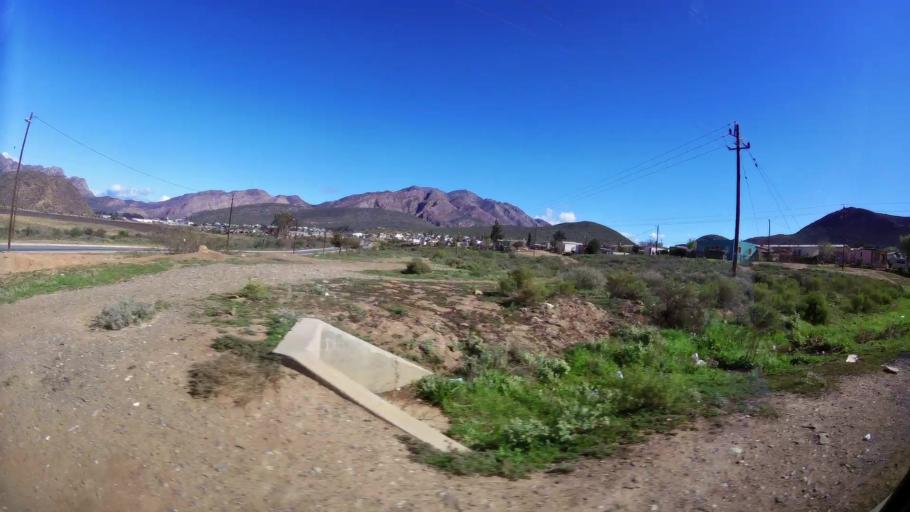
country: ZA
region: Western Cape
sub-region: Cape Winelands District Municipality
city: Ashton
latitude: -33.7687
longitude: 20.1497
